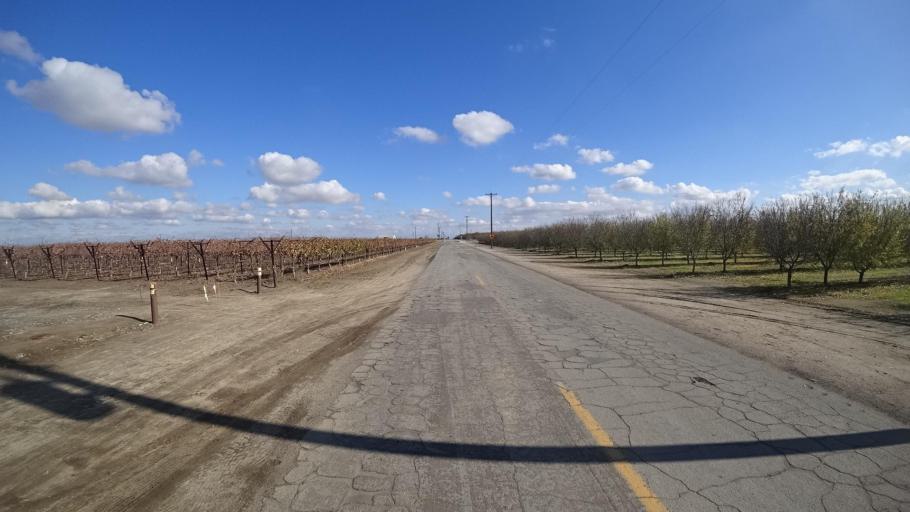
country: US
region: California
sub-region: Kern County
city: Delano
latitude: 35.7322
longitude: -119.3378
